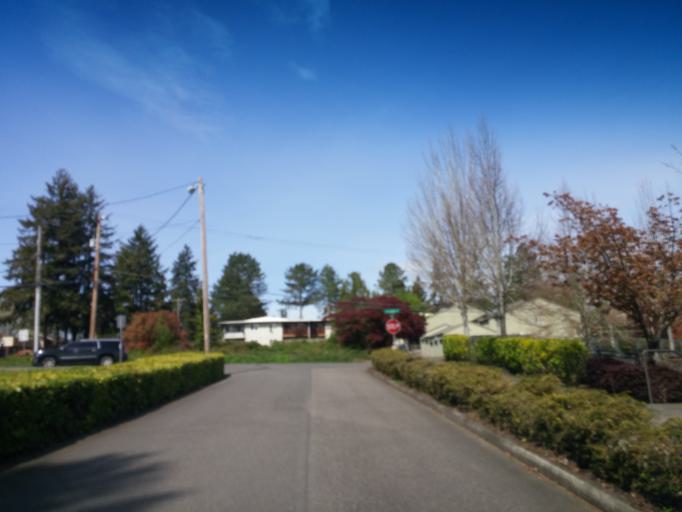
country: US
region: Oregon
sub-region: Washington County
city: Cedar Mill
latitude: 45.5257
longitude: -122.8038
